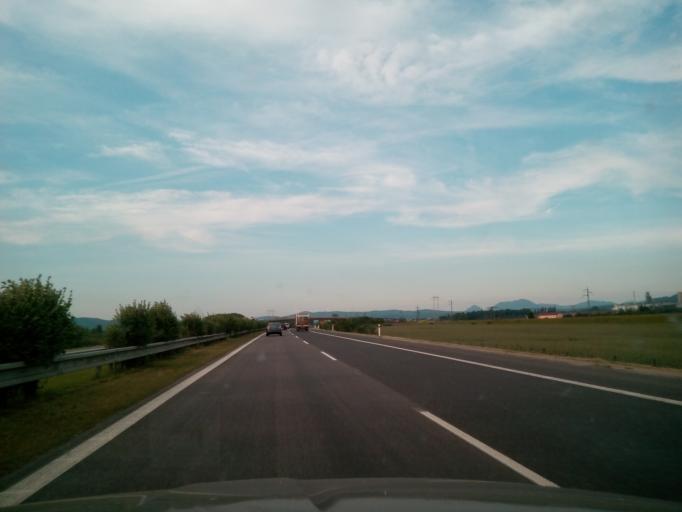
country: SK
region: Nitriansky
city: Ilava
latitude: 49.0255
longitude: 18.2631
